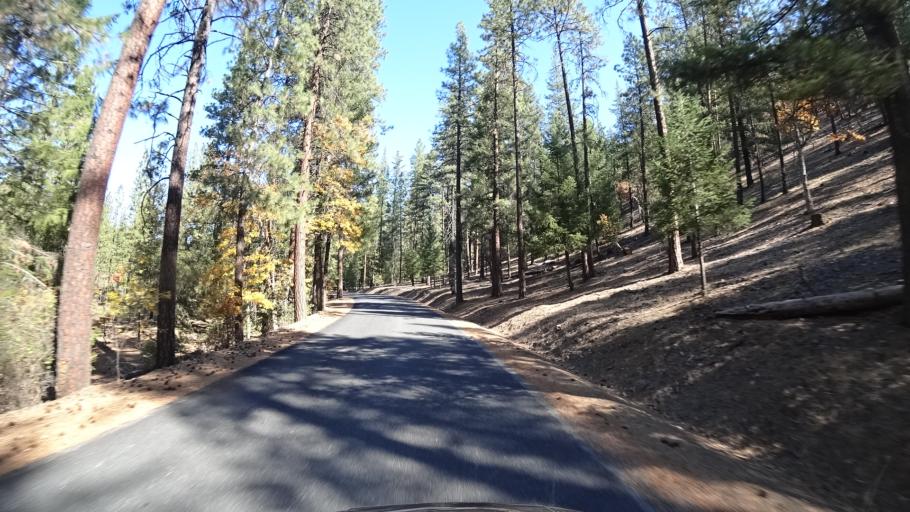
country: US
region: California
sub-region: Siskiyou County
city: Yreka
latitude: 41.6523
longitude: -122.8617
